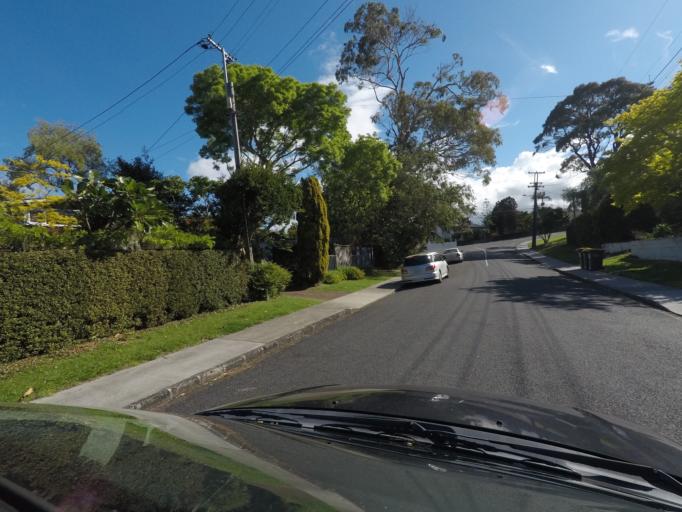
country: NZ
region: Auckland
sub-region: Auckland
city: Rosebank
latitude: -36.8592
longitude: 174.6532
